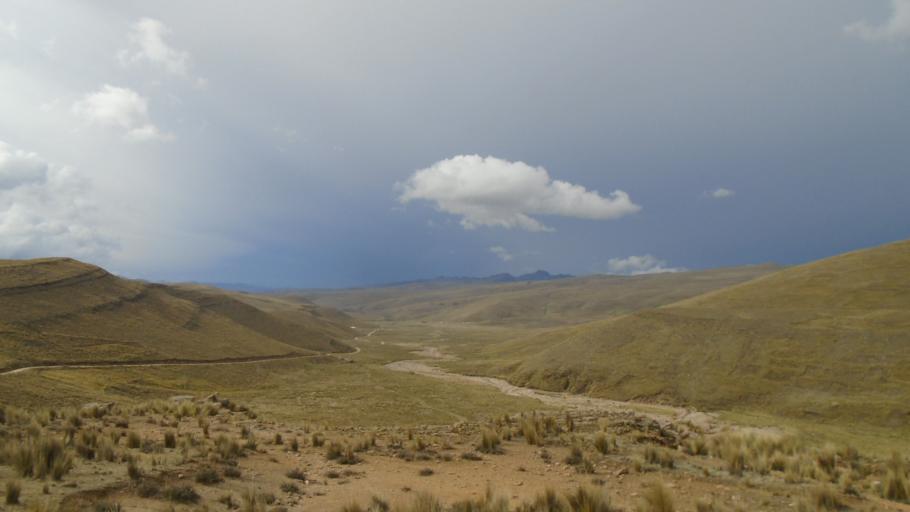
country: BO
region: Cochabamba
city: Cochabamba
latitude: -17.2411
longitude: -66.2329
